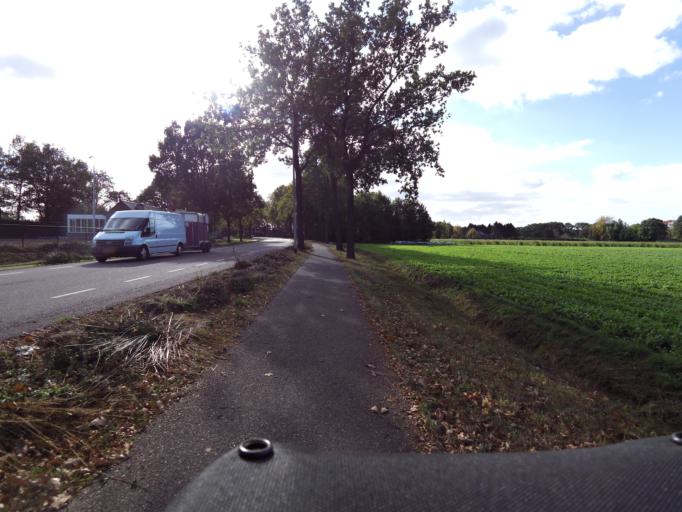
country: NL
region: North Brabant
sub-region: Gemeente Bergen op Zoom
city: Lepelstraat
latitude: 51.5493
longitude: 4.2892
